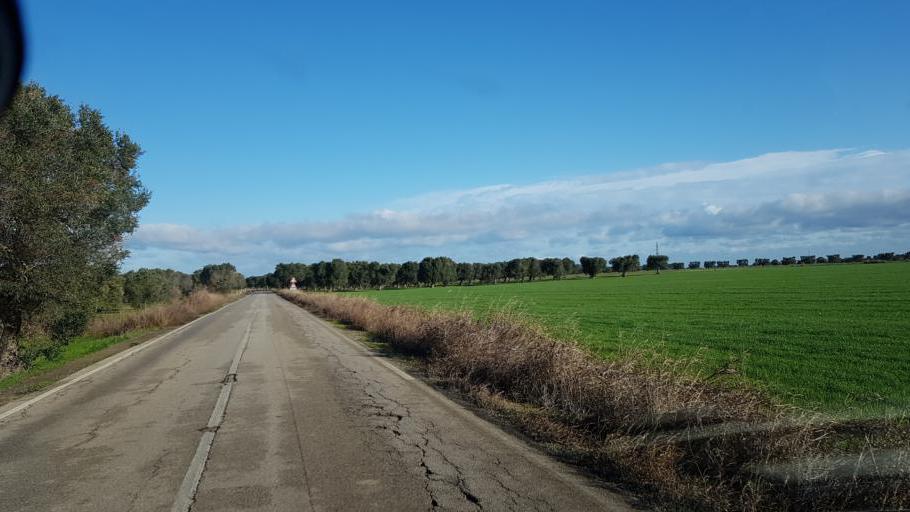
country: IT
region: Apulia
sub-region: Provincia di Brindisi
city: Tuturano
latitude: 40.5614
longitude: 17.9483
